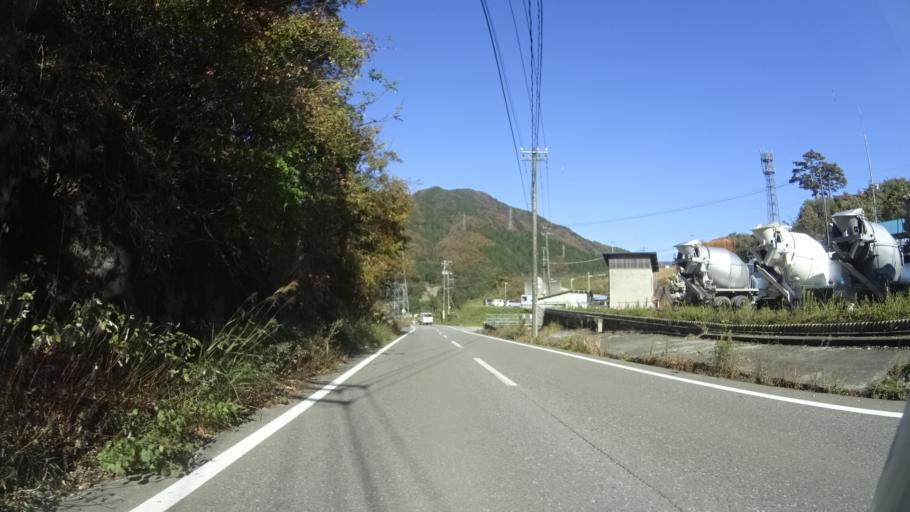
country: JP
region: Fukui
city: Ono
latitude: 35.9943
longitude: 136.3611
